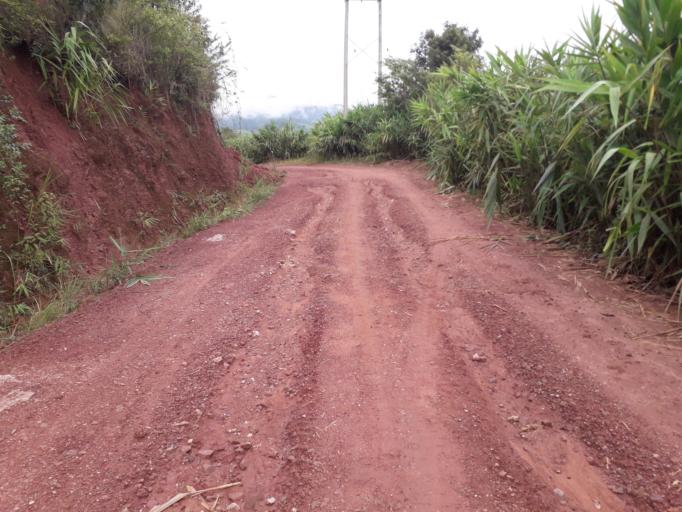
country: CN
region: Yunnan
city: Menglie
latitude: 22.2642
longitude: 101.5796
